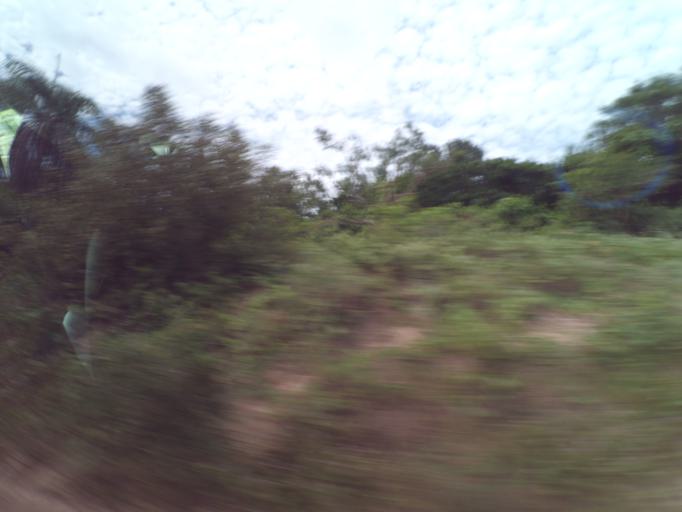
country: BO
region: Santa Cruz
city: Santa Cruz de la Sierra
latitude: -17.9100
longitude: -63.1661
